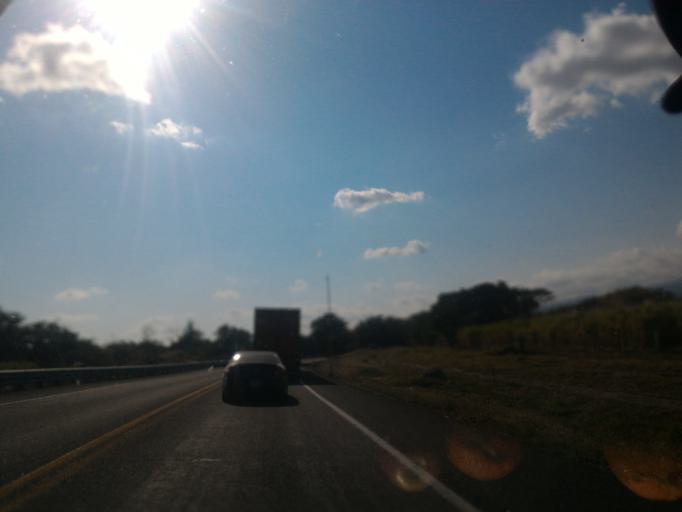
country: MX
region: Jalisco
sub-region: Tonila
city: San Marcos
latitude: 19.4352
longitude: -103.4825
